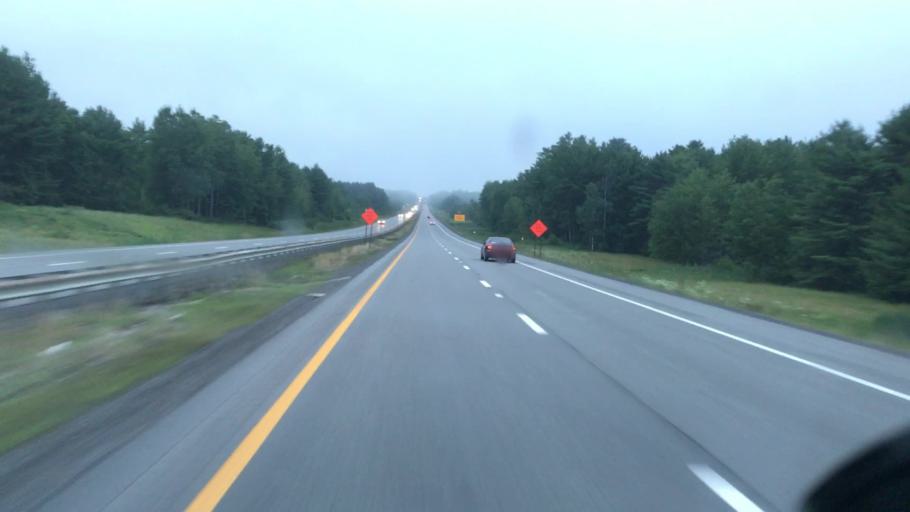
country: US
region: Maine
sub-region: Cumberland County
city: New Gloucester
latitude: 43.9020
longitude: -70.3411
